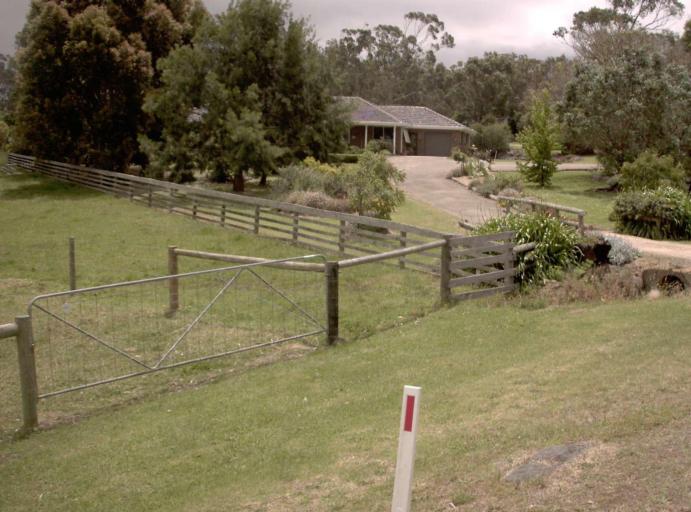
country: AU
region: Victoria
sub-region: Latrobe
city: Traralgon
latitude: -38.5433
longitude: 146.6561
